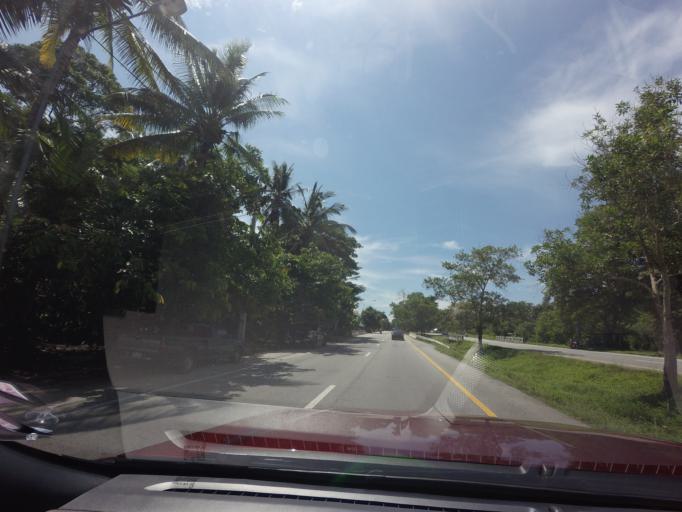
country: TH
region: Narathiwat
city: Bacho
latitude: 6.5648
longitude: 101.6402
